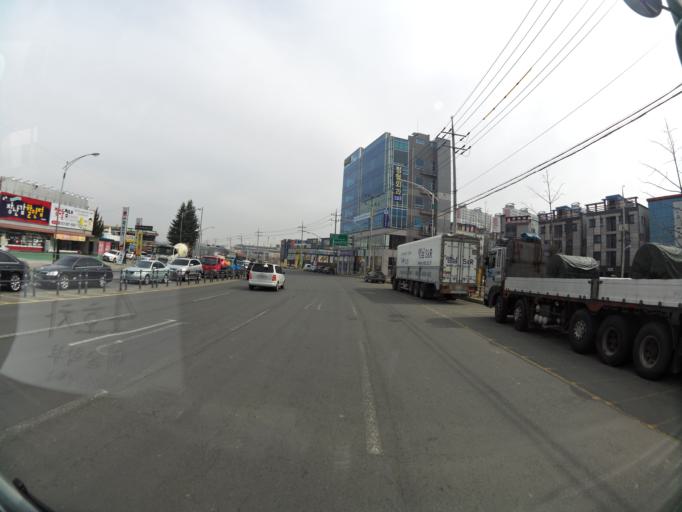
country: KR
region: Gyeongsangbuk-do
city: Gyeongsan-si
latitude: 35.8417
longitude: 128.7618
